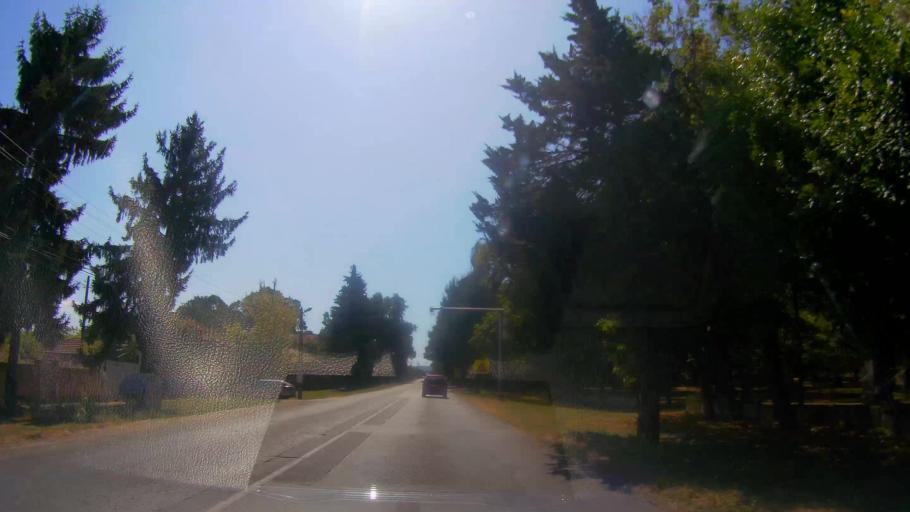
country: BG
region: Veliko Turnovo
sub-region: Obshtina Gorna Oryakhovitsa
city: Purvomaytsi
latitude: 43.1806
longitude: 25.6195
